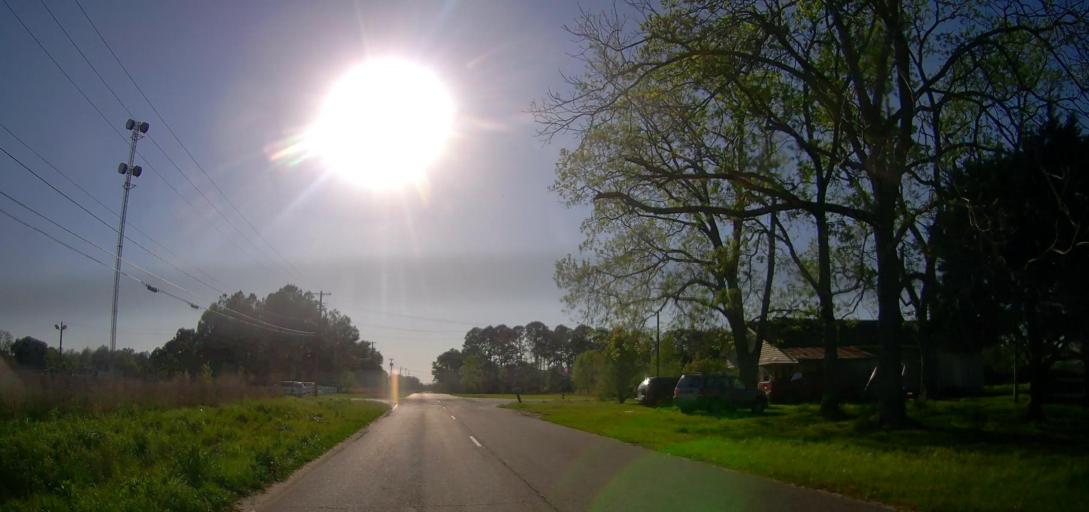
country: US
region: Georgia
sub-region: Ben Hill County
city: Fitzgerald
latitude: 31.7287
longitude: -83.2798
